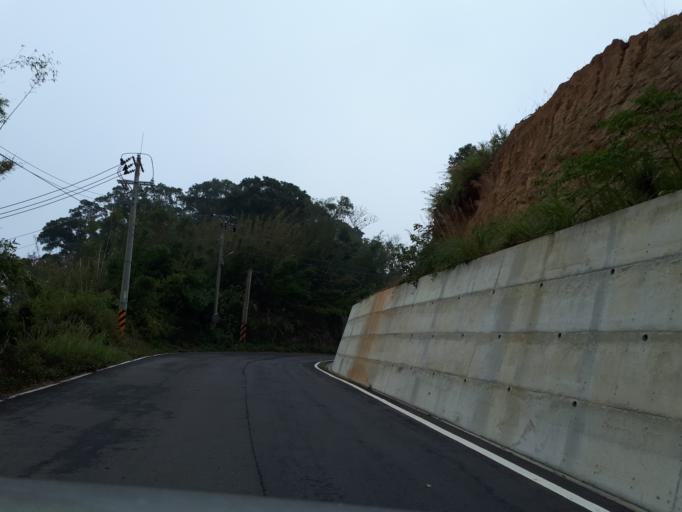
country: TW
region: Taiwan
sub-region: Hsinchu
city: Zhubei
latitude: 24.7351
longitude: 121.0788
